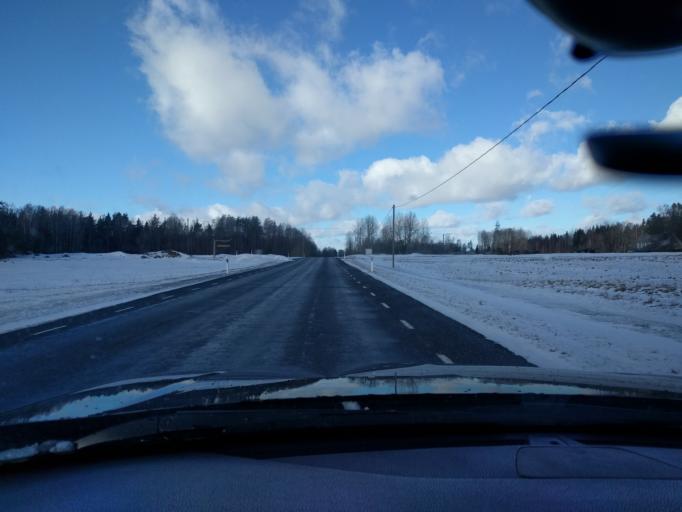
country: EE
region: Harju
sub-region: Anija vald
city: Kehra
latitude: 59.2242
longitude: 25.4058
